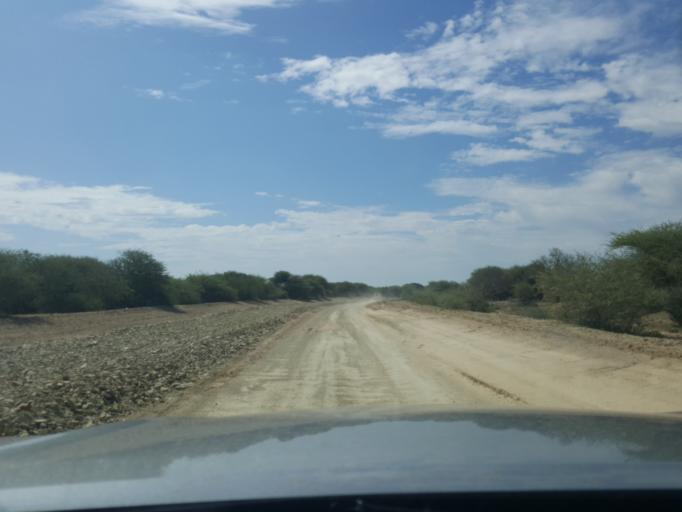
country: BW
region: Kweneng
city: Letlhakeng
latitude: -23.9808
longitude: 24.9670
